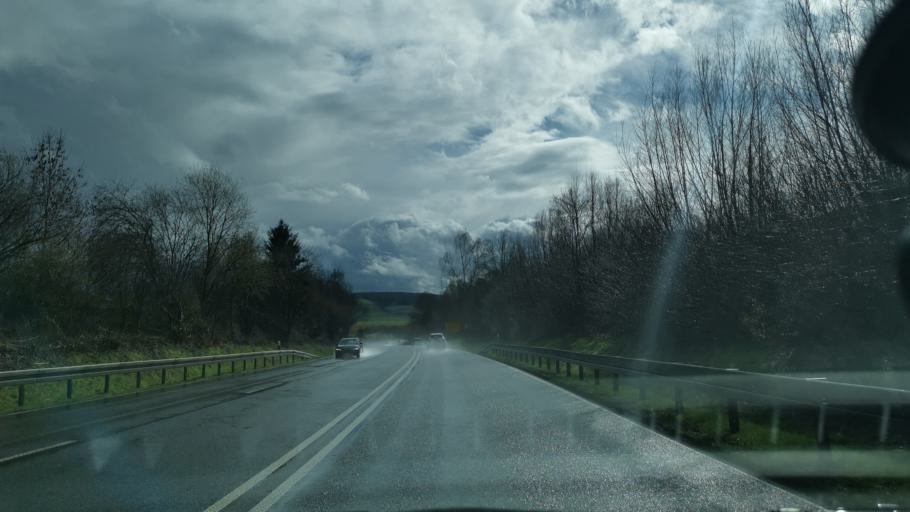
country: DE
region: Hesse
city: Breitenbach
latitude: 50.9367
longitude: 9.7710
